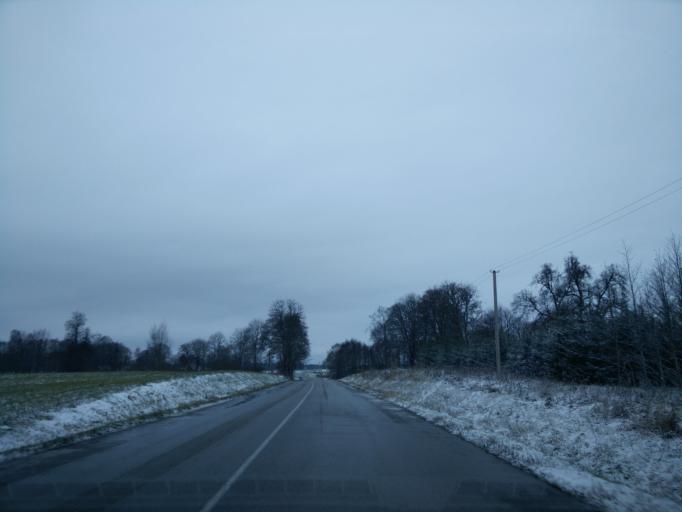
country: LT
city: Tytuveneliai
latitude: 55.5065
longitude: 23.2964
